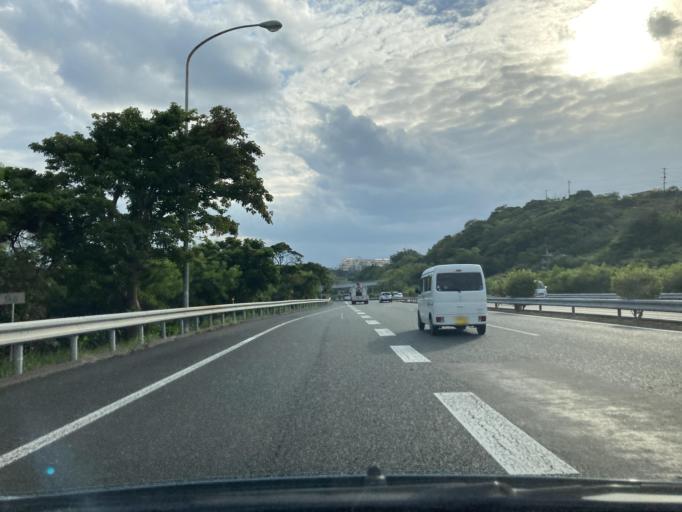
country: JP
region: Okinawa
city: Ginowan
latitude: 26.2735
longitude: 127.7789
